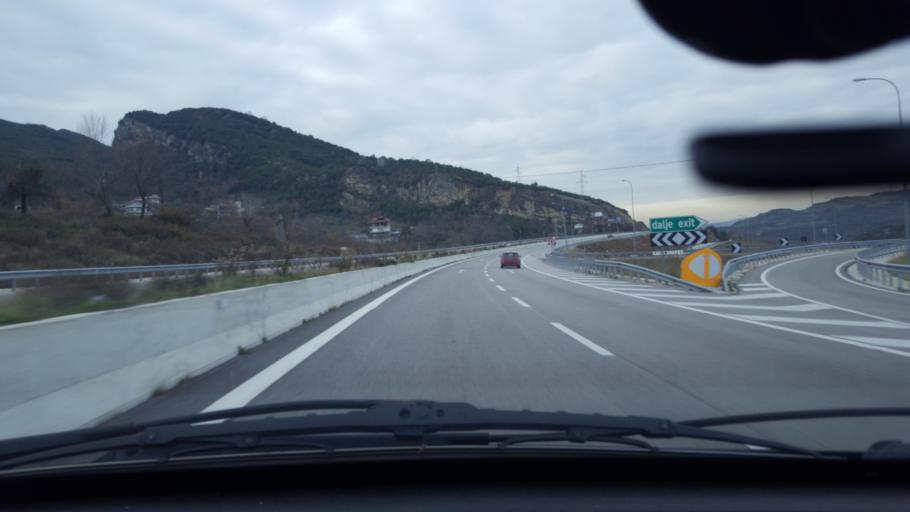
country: AL
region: Tirane
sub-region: Rrethi i Tiranes
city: Berzhite
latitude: 41.2271
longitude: 19.9330
